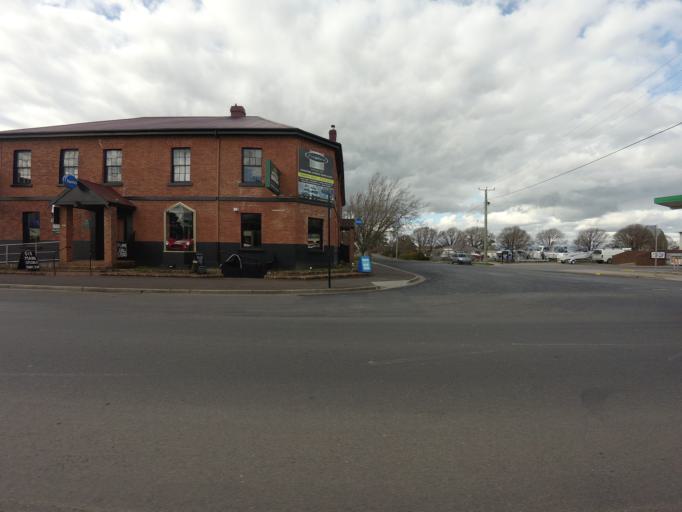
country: AU
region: Tasmania
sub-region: Northern Midlands
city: Longford
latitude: -41.5891
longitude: 147.1202
